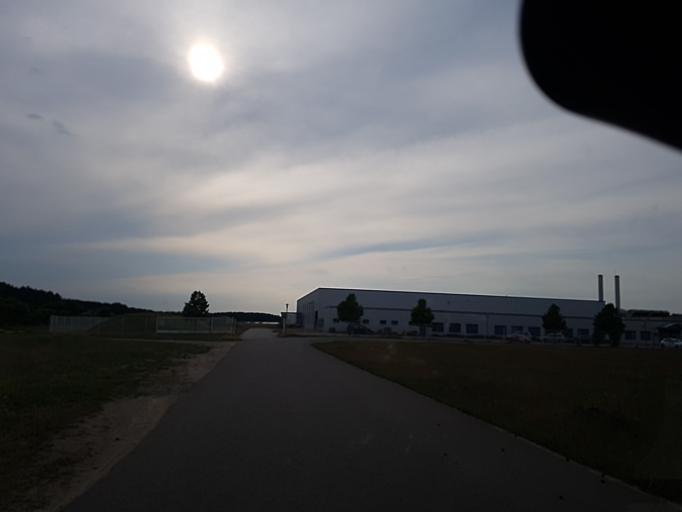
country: DE
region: Saxony-Anhalt
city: Jessen
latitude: 51.7971
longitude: 12.9378
